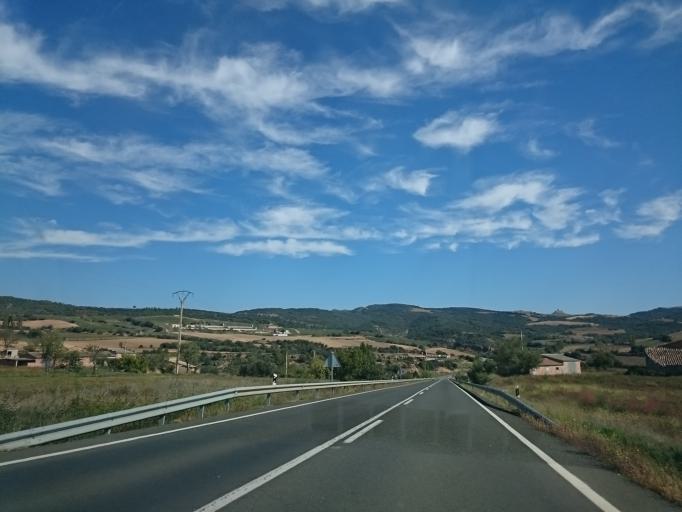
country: ES
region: Aragon
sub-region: Provincia de Huesca
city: Benavarri / Benabarre
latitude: 42.1168
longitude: 0.5641
